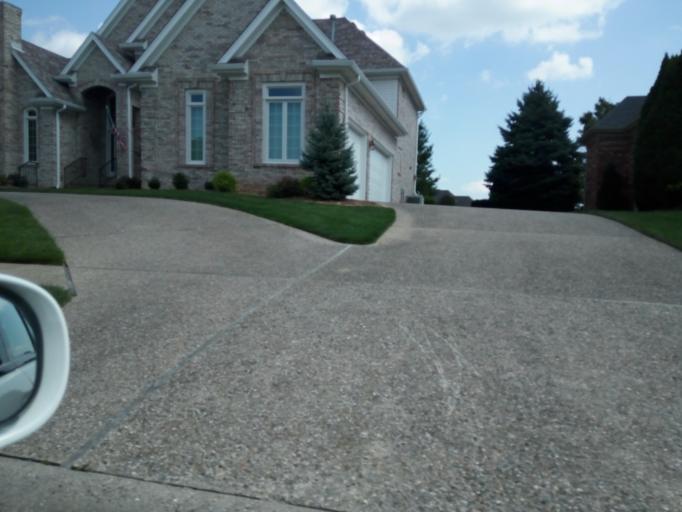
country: US
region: Kentucky
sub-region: Oldham County
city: Pewee Valley
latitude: 38.2717
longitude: -85.4785
